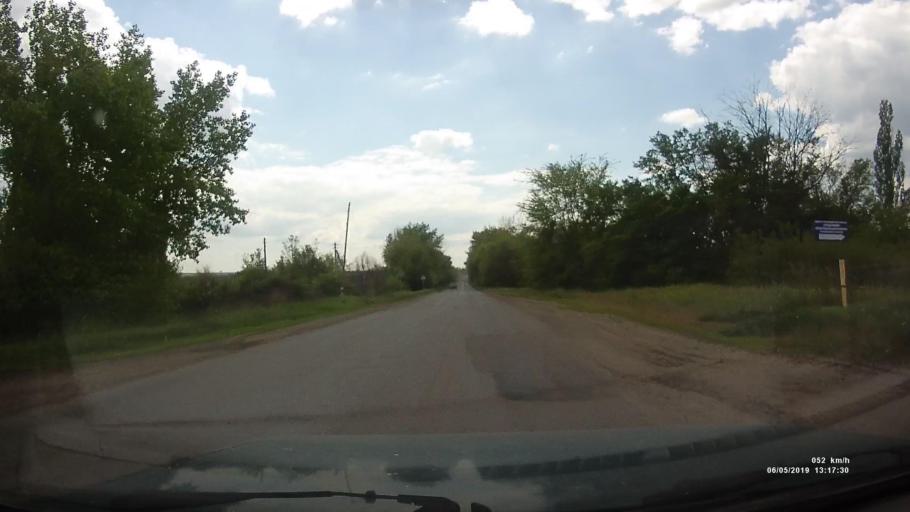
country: RU
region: Rostov
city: Ust'-Donetskiy
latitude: 47.7398
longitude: 40.9225
